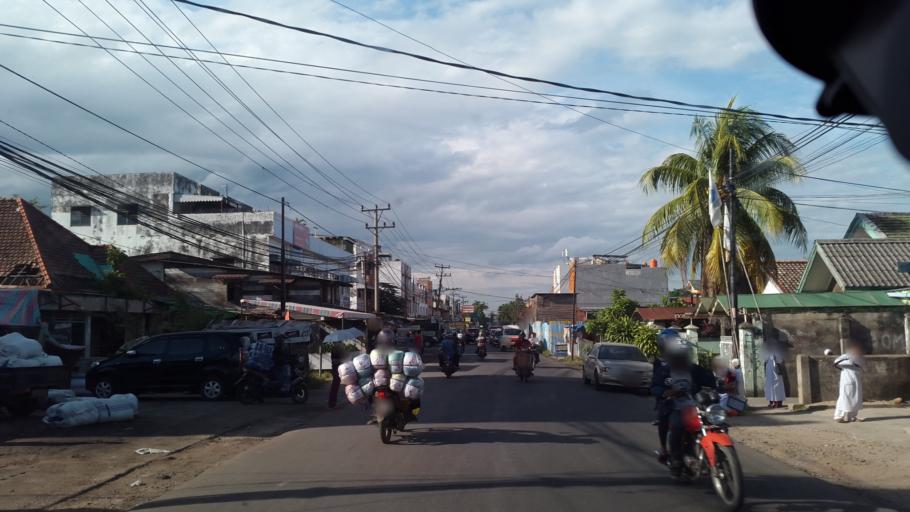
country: ID
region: South Sumatra
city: Plaju
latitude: -2.9788
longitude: 104.7712
